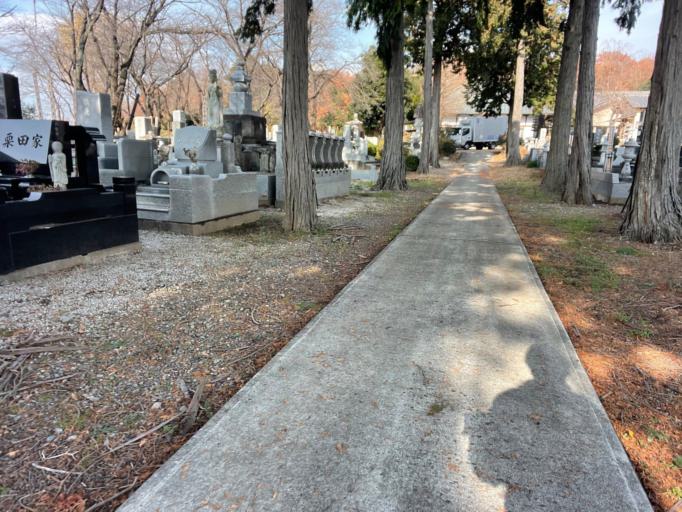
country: JP
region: Saitama
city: Yorii
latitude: 36.1574
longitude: 139.1885
